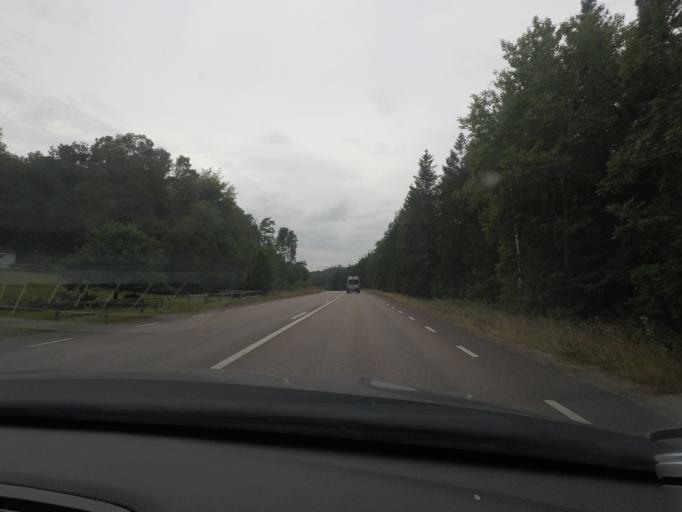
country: SE
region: Halland
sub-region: Laholms Kommun
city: Knared
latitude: 56.5291
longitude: 13.2351
